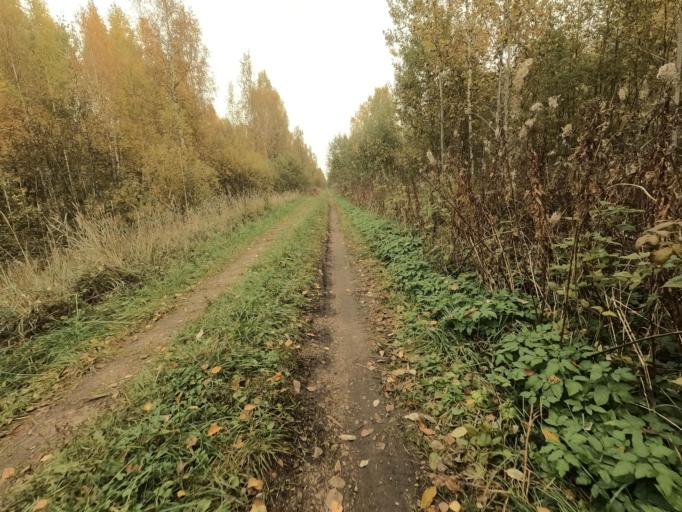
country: RU
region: Novgorod
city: Pankovka
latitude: 58.8891
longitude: 30.9486
